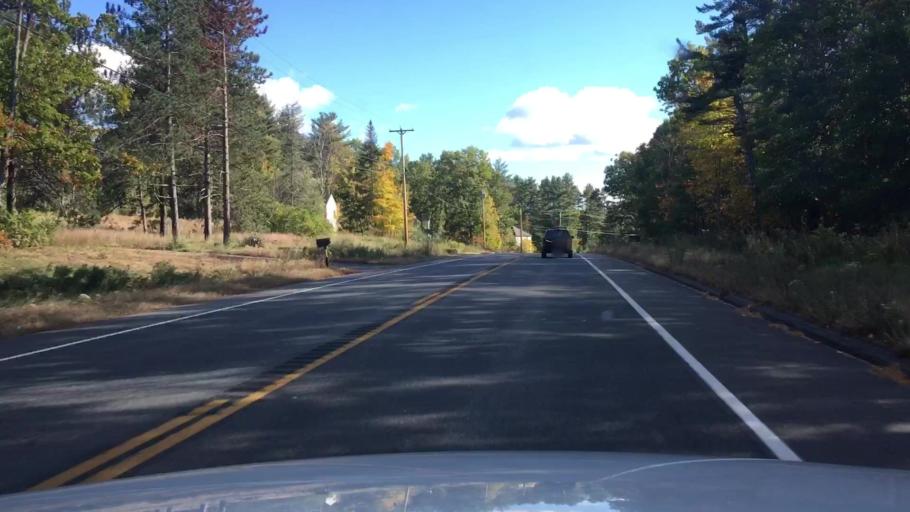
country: US
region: Maine
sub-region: York County
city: South Sanford
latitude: 43.3687
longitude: -70.6714
